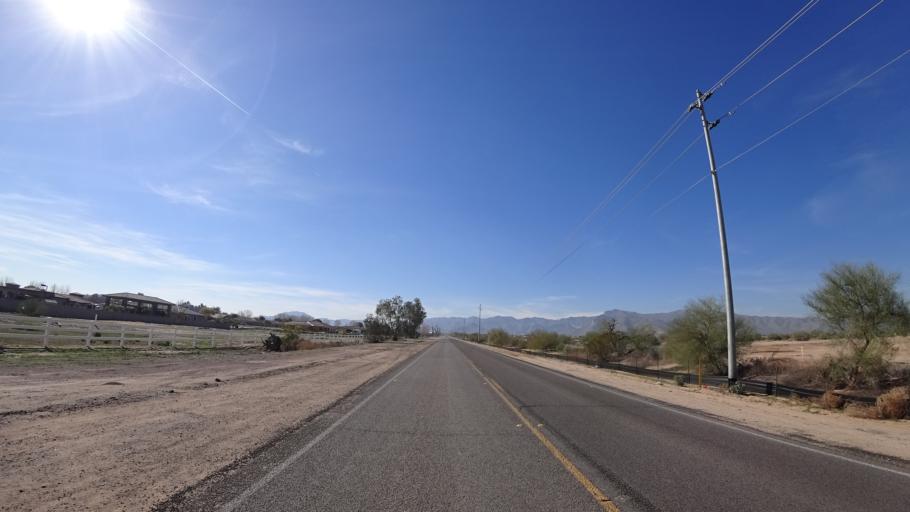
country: US
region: Arizona
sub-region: Maricopa County
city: Citrus Park
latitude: 33.5082
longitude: -112.4622
